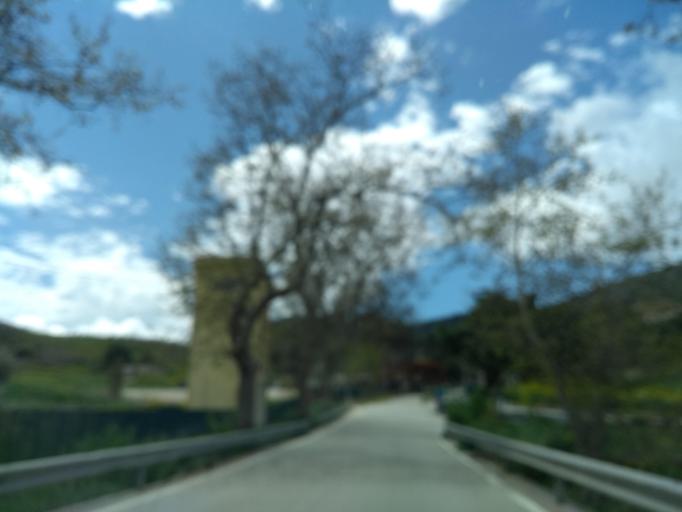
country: IT
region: Sicily
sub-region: Trapani
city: Calatafimi
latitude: 37.9424
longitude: 12.8368
